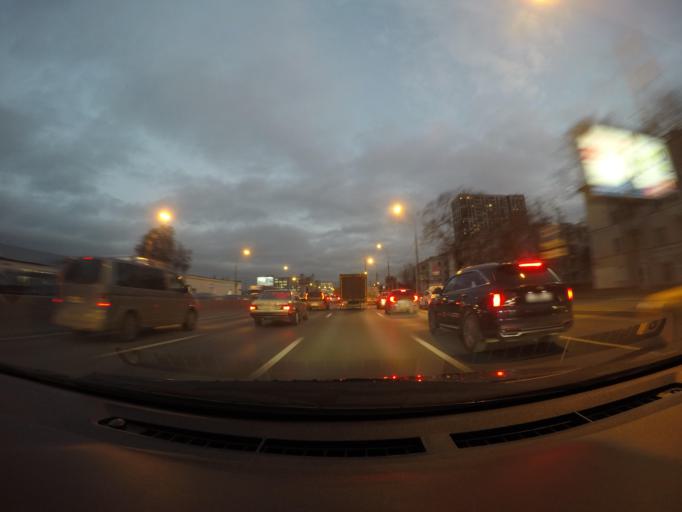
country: RU
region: Moscow
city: Kolomenskoye
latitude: 55.6440
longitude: 37.6761
